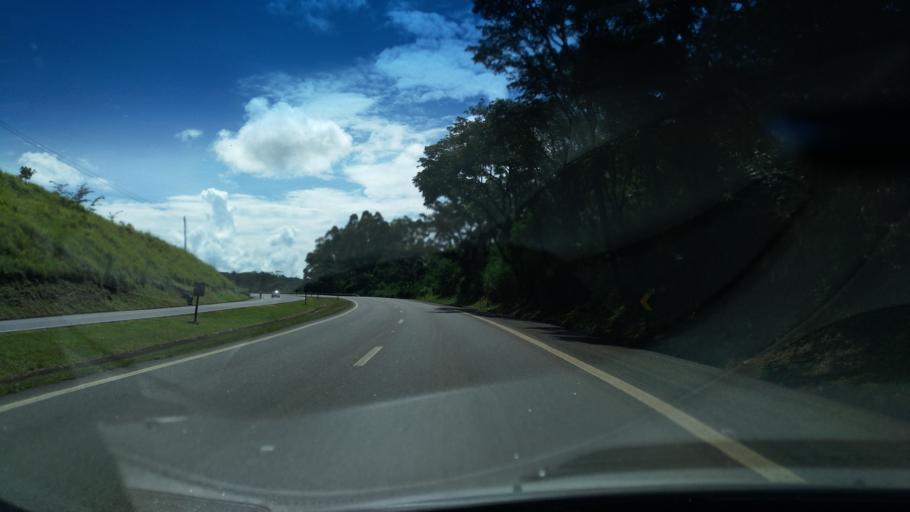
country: BR
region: Sao Paulo
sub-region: Santo Antonio Do Jardim
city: Espirito Santo do Pinhal
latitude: -22.2191
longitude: -46.7870
